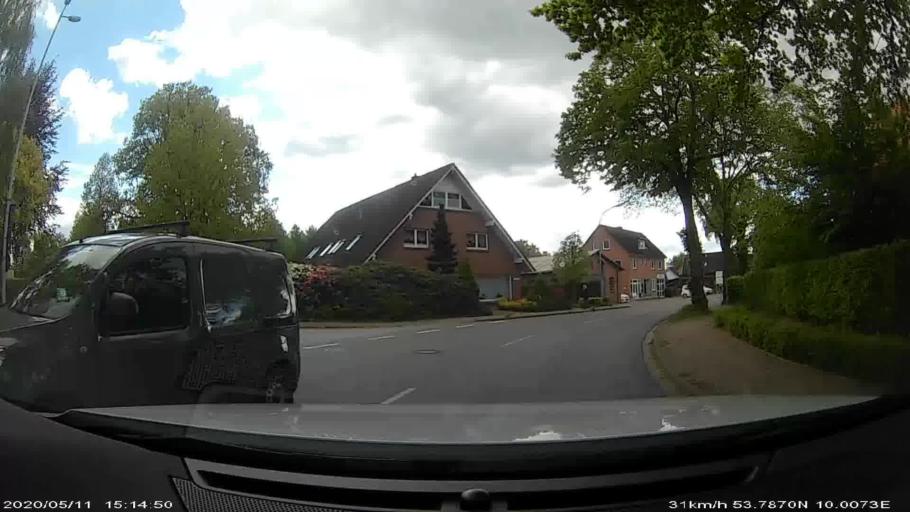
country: DE
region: Schleswig-Holstein
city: Henstedt-Ulzburg
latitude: 53.7897
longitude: 9.9976
